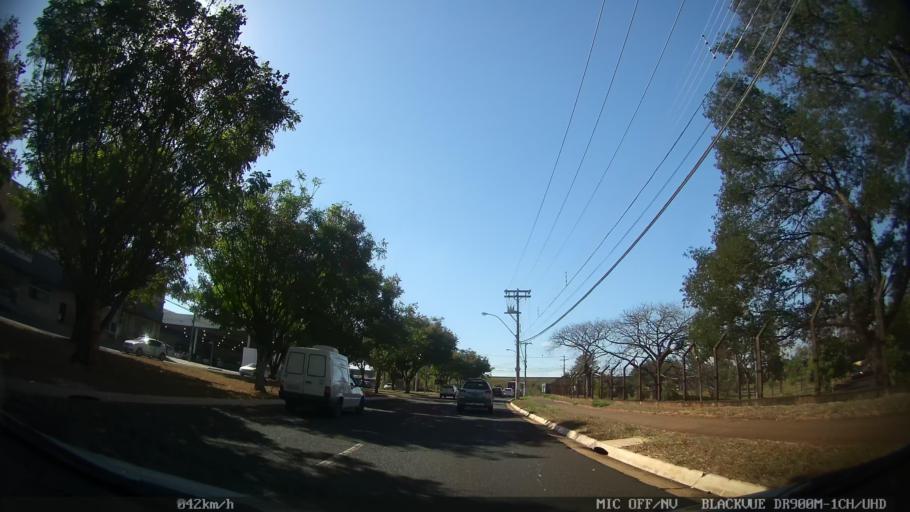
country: BR
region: Sao Paulo
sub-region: Ribeirao Preto
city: Ribeirao Preto
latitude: -21.2016
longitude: -47.7676
